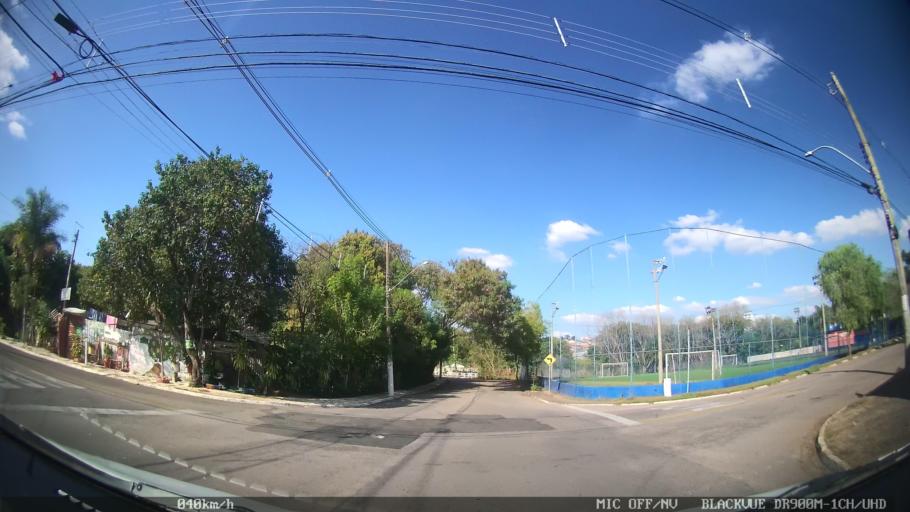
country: BR
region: Sao Paulo
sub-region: Sumare
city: Sumare
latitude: -22.8181
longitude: -47.2804
